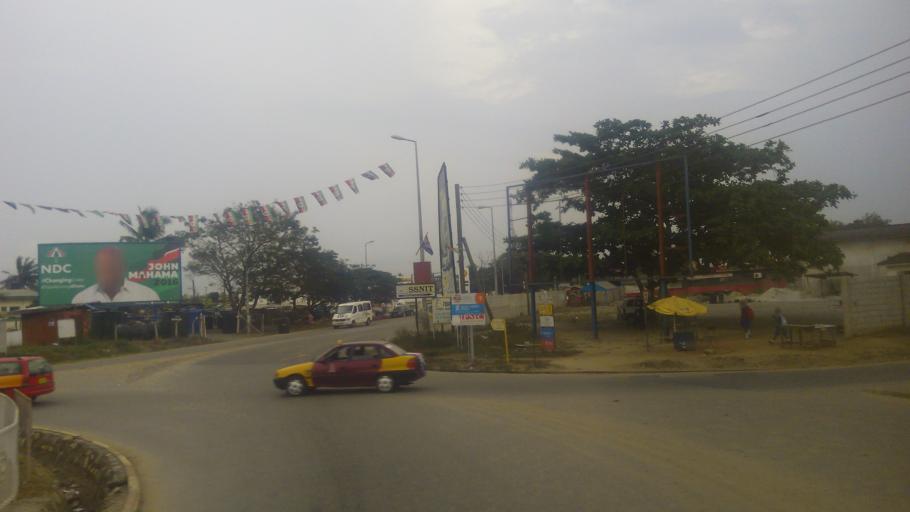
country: GH
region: Western
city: Takoradi
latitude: 4.8865
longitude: -1.7598
